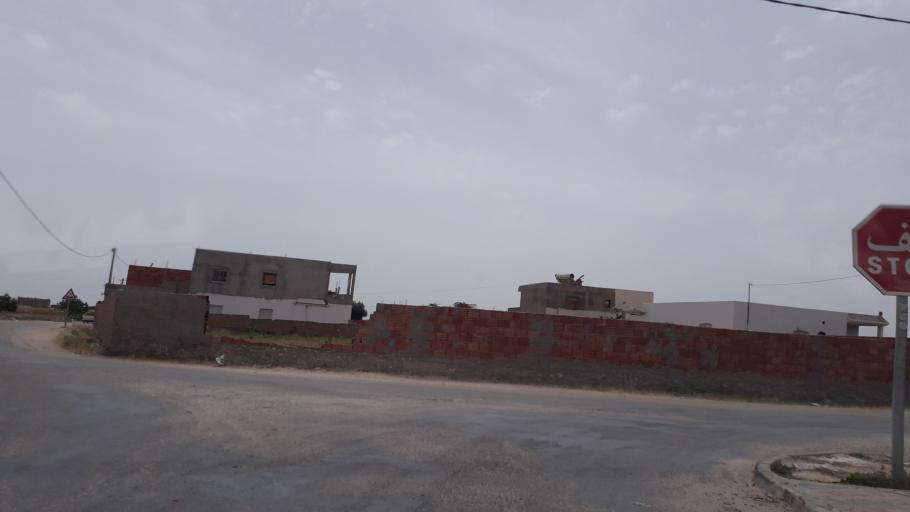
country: TN
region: Safaqis
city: Al Qarmadah
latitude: 34.8430
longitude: 10.7787
